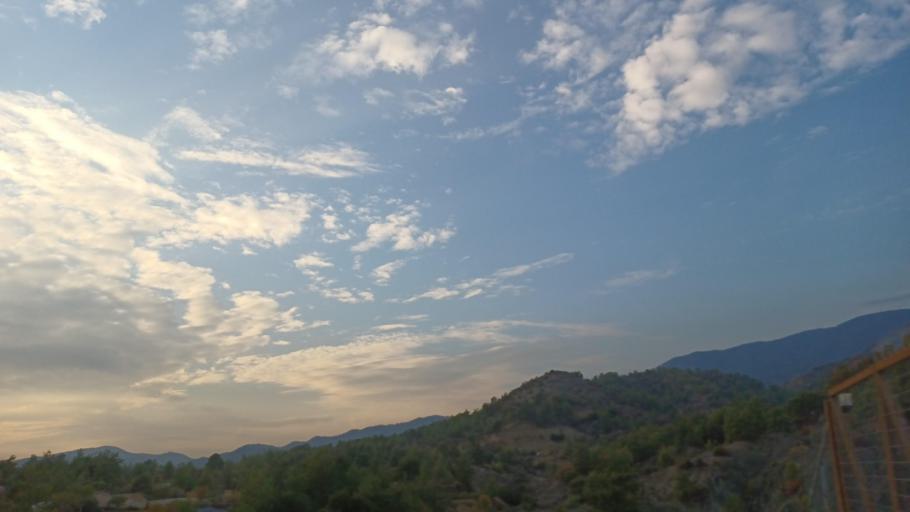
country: CY
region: Limassol
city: Pelendri
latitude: 34.8584
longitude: 32.9351
